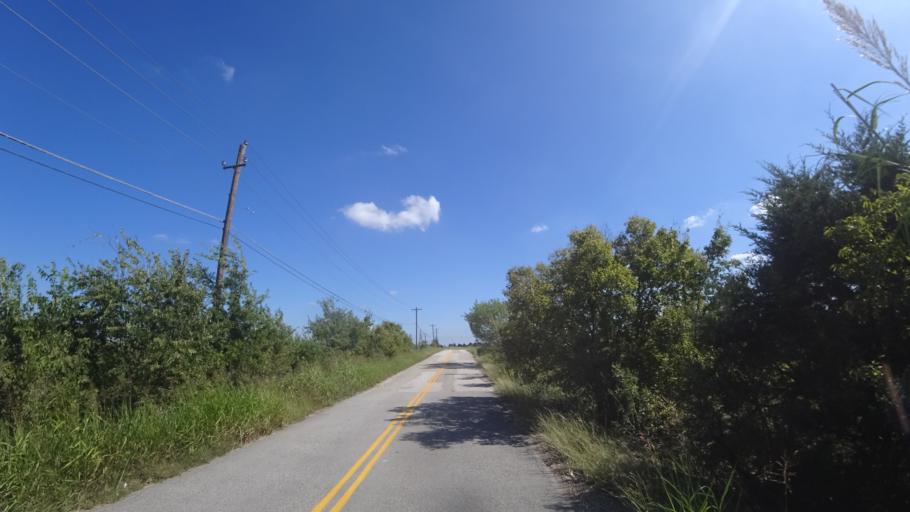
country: US
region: Texas
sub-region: Travis County
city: Manor
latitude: 30.3382
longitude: -97.6047
